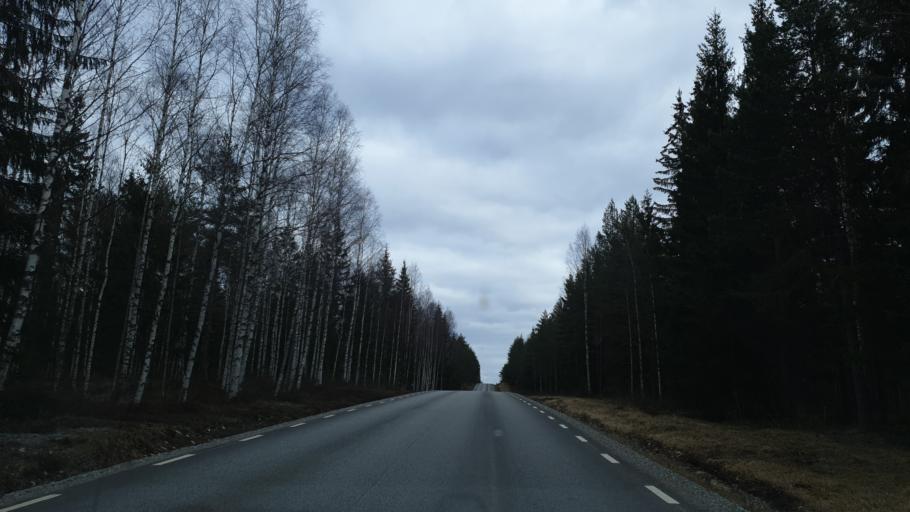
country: SE
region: OErebro
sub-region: Nora Kommun
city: Nora
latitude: 59.6175
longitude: 15.0544
